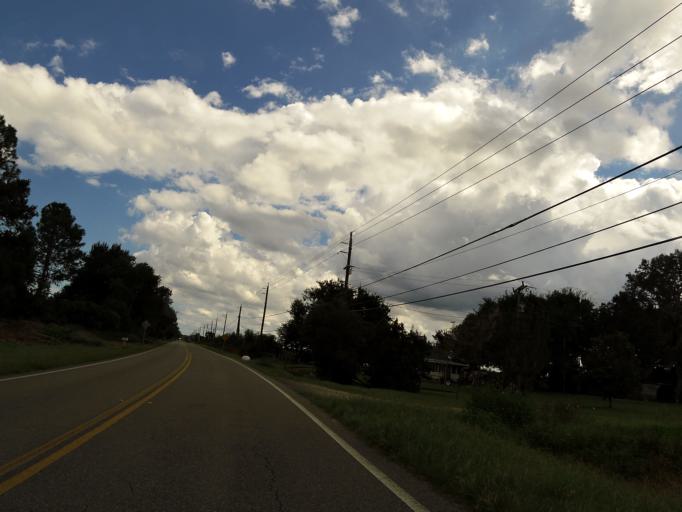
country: US
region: Florida
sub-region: Saint Johns County
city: Saint Augustine South
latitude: 29.8365
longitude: -81.5004
